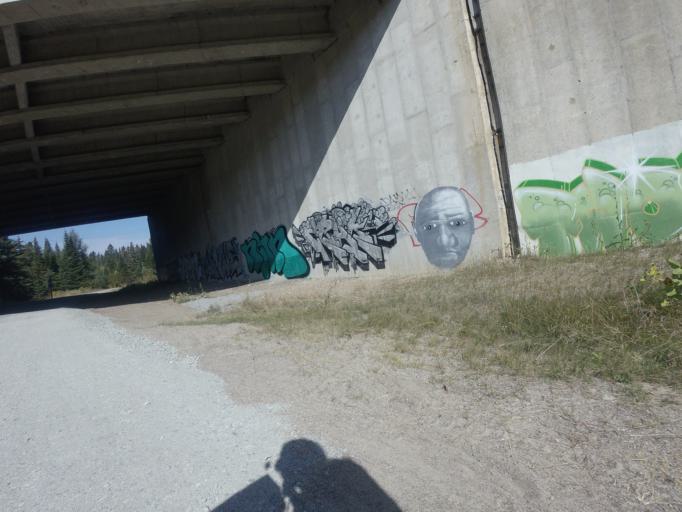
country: CA
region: Quebec
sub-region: Laurentides
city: Sainte-Agathe-des-Monts
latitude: 46.0979
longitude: -74.3627
